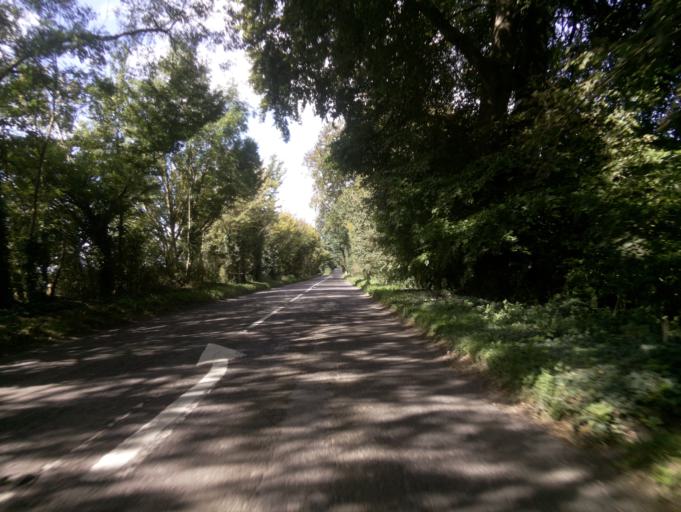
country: GB
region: England
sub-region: Wiltshire
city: Market Lavington
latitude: 51.2514
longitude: -1.9837
